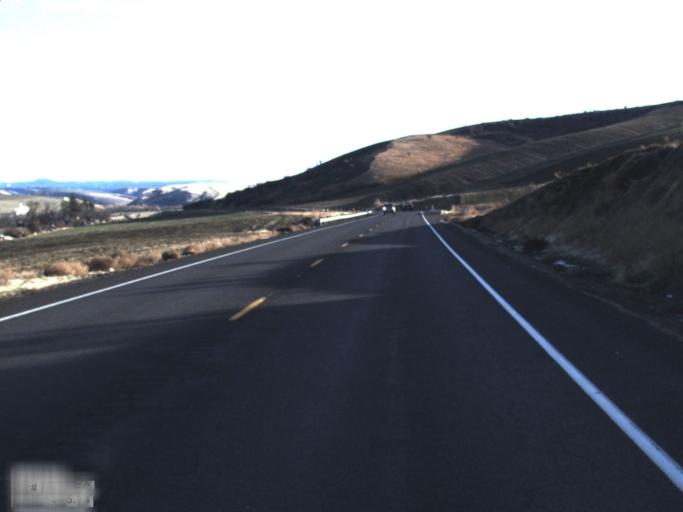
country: US
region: Washington
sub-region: Walla Walla County
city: Waitsburg
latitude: 46.2446
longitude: -118.1452
